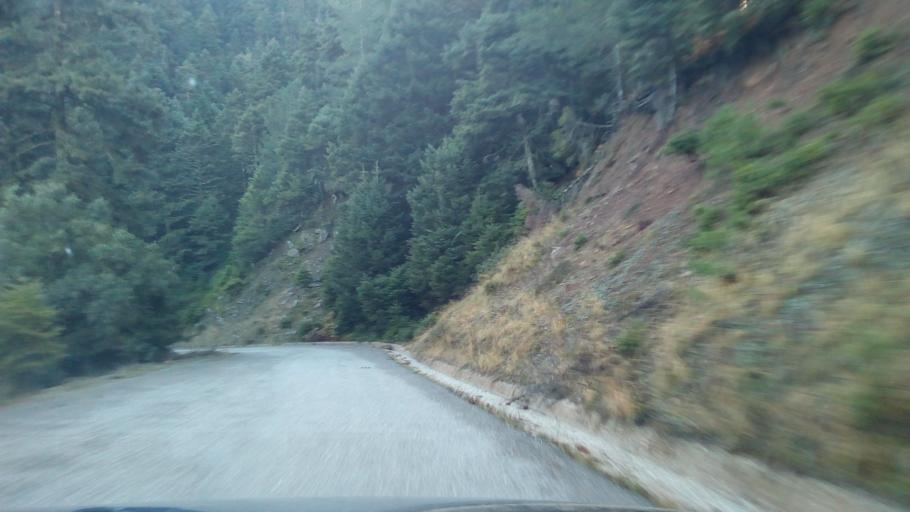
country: GR
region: West Greece
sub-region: Nomos Aitolias kai Akarnanias
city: Nafpaktos
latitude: 38.5354
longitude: 21.8456
